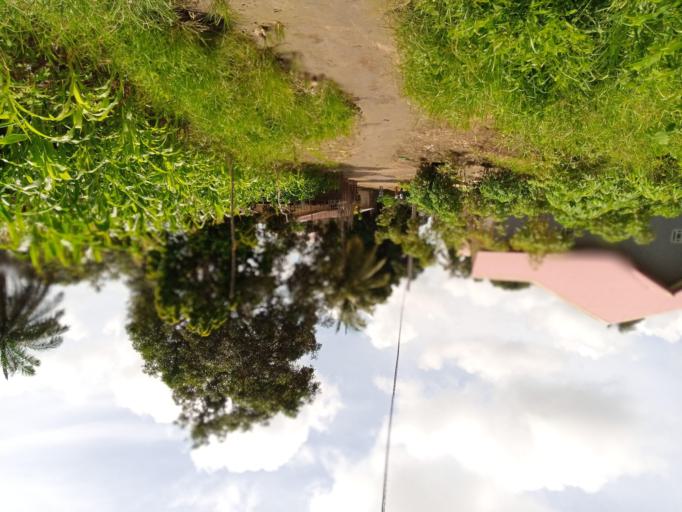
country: SL
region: Northern Province
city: Masoyila
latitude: 8.6042
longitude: -13.1817
